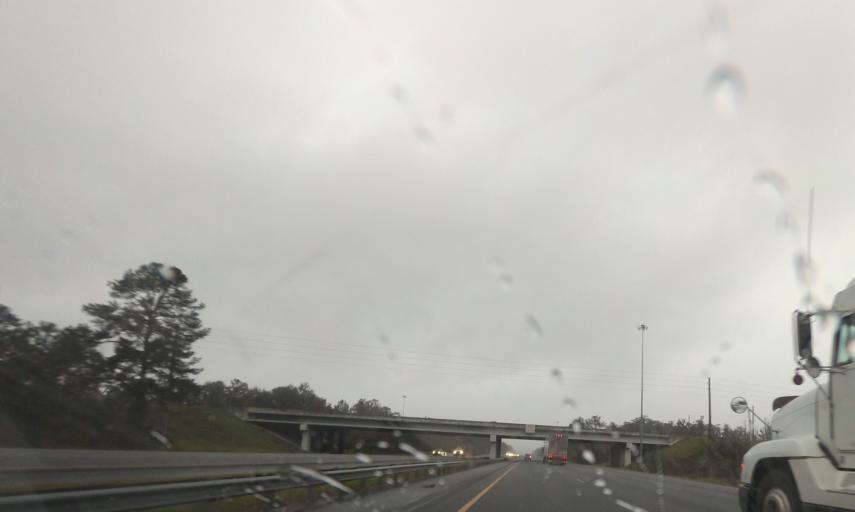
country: US
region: Georgia
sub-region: Lowndes County
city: Valdosta
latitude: 30.7764
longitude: -83.2951
